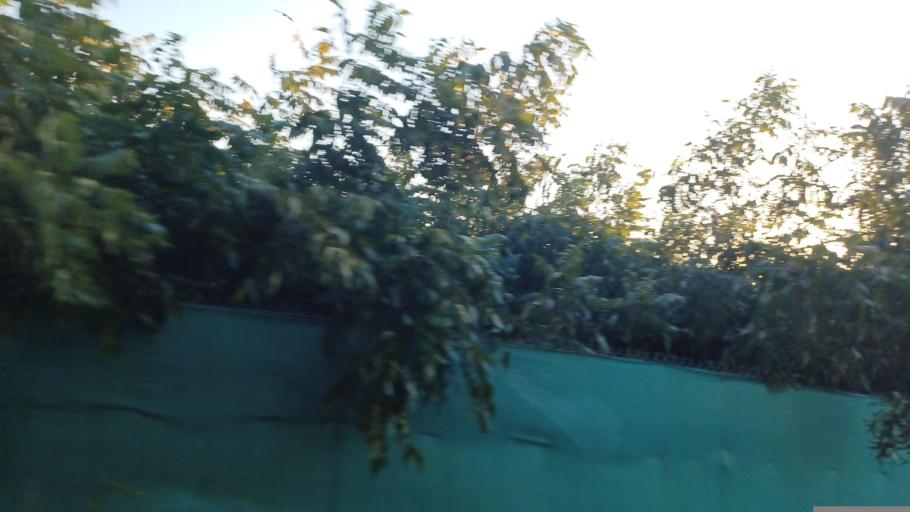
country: CY
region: Pafos
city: Pegeia
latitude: 34.8673
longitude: 32.3574
